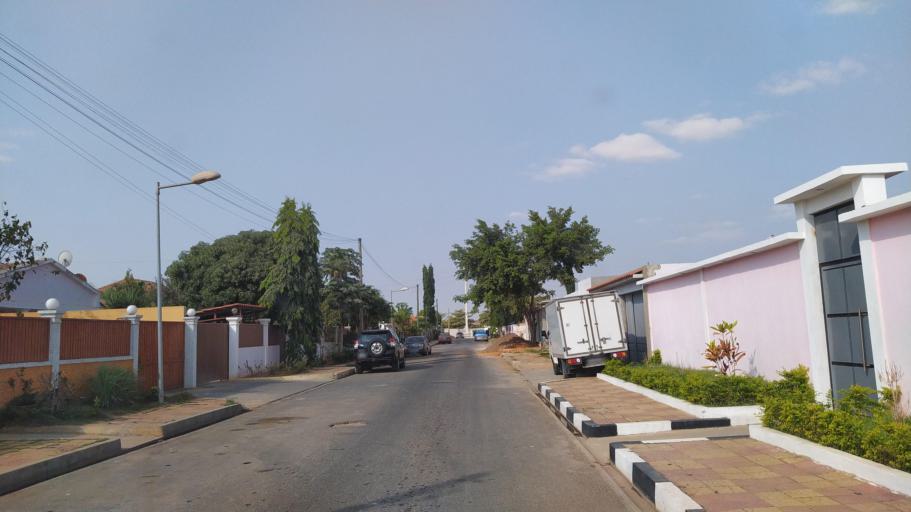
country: AO
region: Luanda
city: Luanda
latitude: -8.8931
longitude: 13.2580
